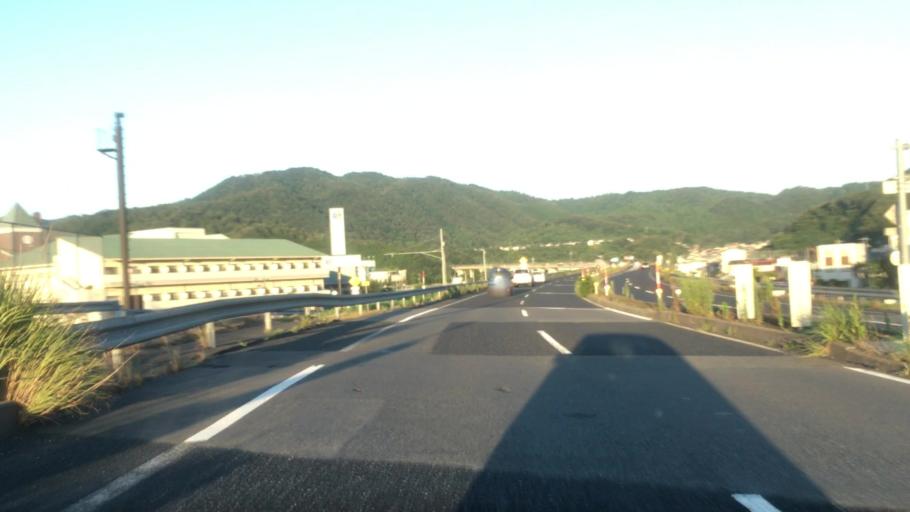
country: JP
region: Tottori
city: Tottori
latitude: 35.5240
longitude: 134.2255
